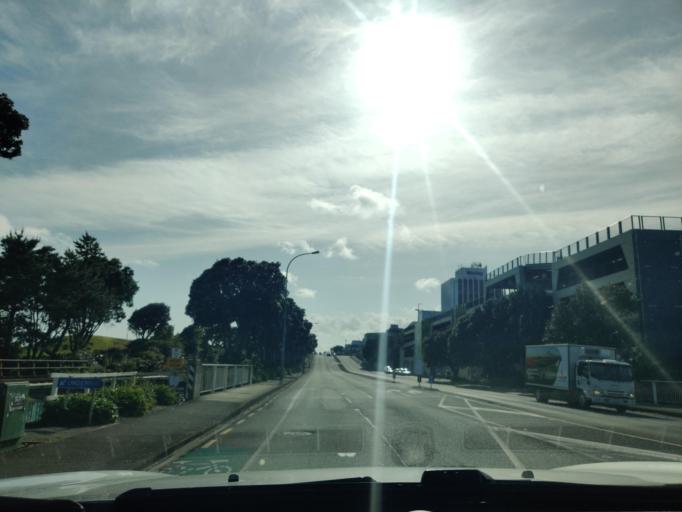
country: NZ
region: Taranaki
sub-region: New Plymouth District
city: New Plymouth
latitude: -39.0564
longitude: 174.0722
